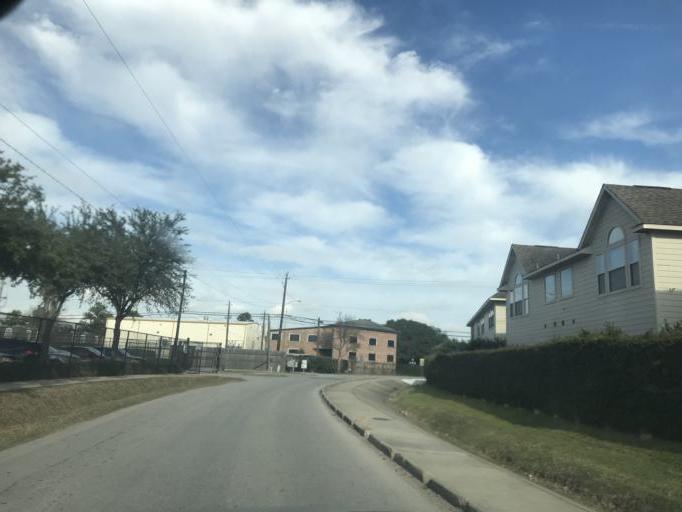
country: US
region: Texas
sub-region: Harris County
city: Piney Point Village
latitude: 29.7288
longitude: -95.4921
